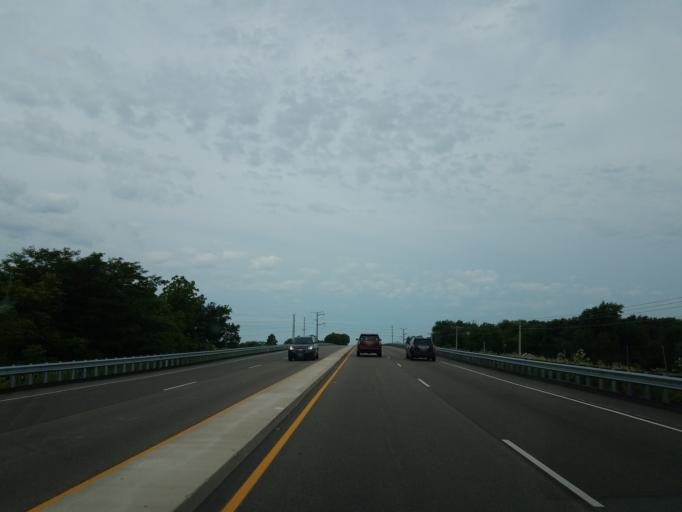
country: US
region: Illinois
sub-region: McLean County
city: Bloomington
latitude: 40.4595
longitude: -88.9795
